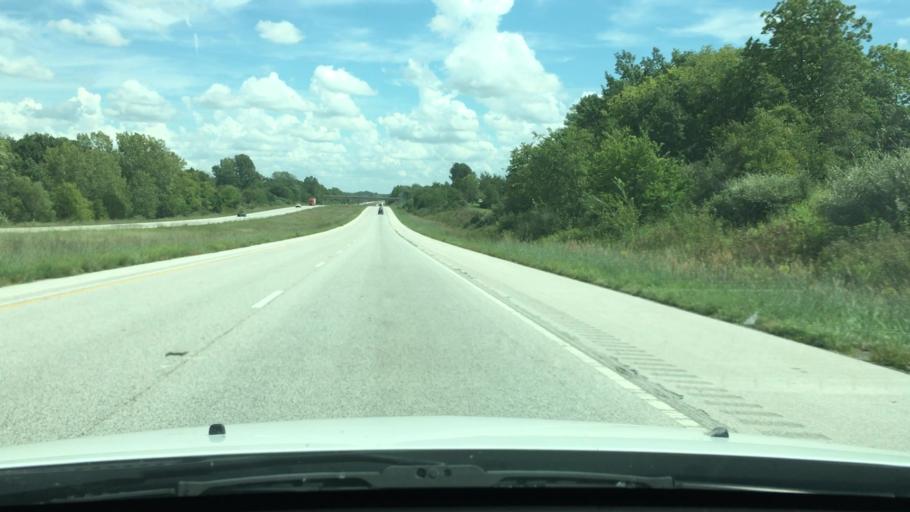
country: US
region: Illinois
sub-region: Scott County
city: Winchester
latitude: 39.6812
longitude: -90.4236
